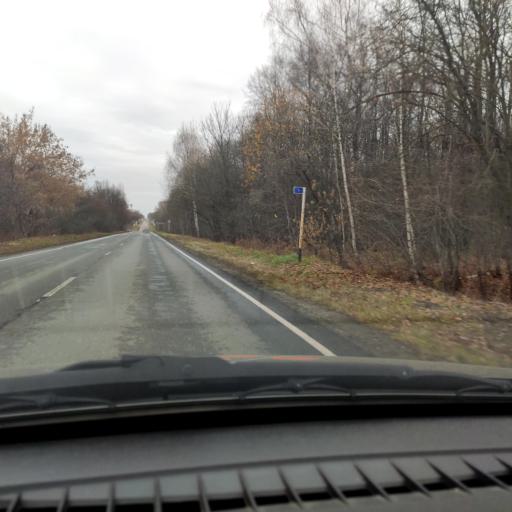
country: RU
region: Samara
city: Zhigulevsk
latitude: 53.3411
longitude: 49.4576
